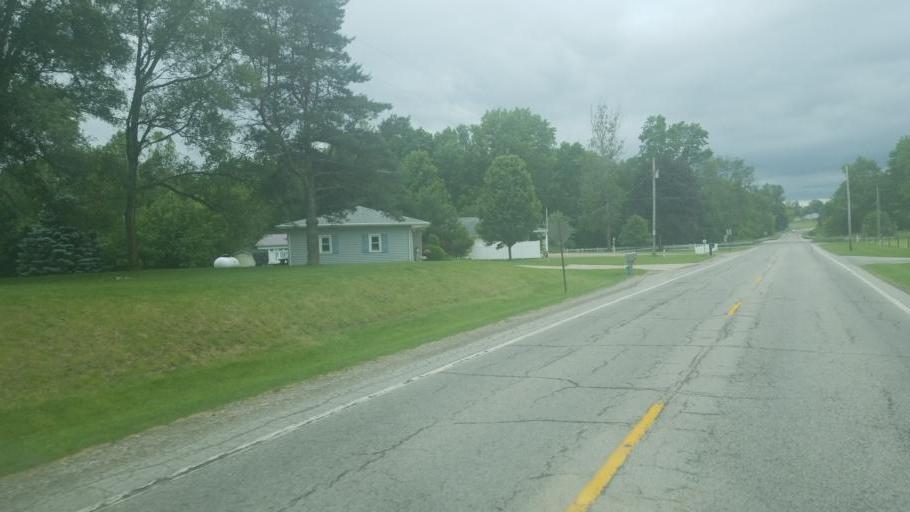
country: US
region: Ohio
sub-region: Richland County
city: Lexington
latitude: 40.6306
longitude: -82.6478
